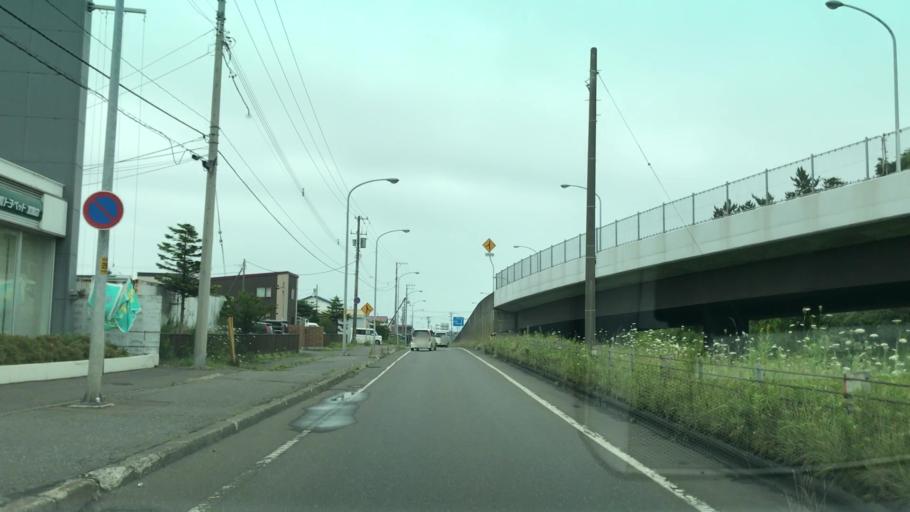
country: JP
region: Hokkaido
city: Muroran
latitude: 42.3530
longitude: 141.0448
